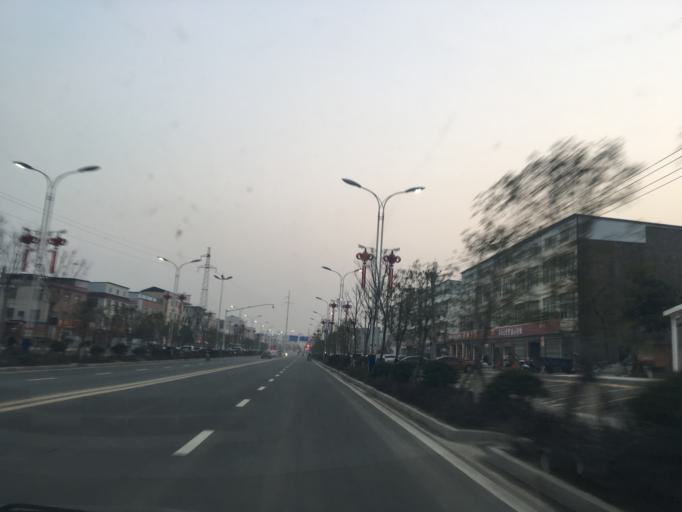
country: CN
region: Hubei
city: Macheng
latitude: 31.1651
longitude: 115.0200
